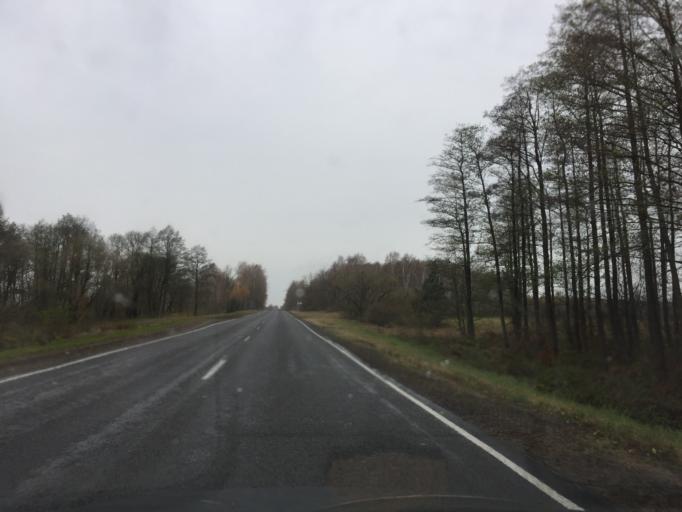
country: BY
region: Mogilev
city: Slawharad
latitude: 53.3490
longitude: 30.8189
